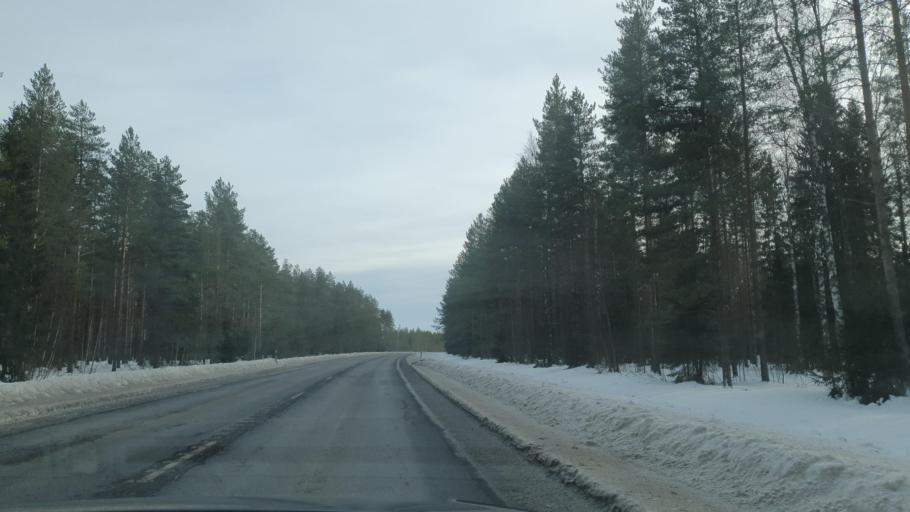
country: FI
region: Northern Ostrobothnia
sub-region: Oulunkaari
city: Utajaervi
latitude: 64.6597
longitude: 26.5537
